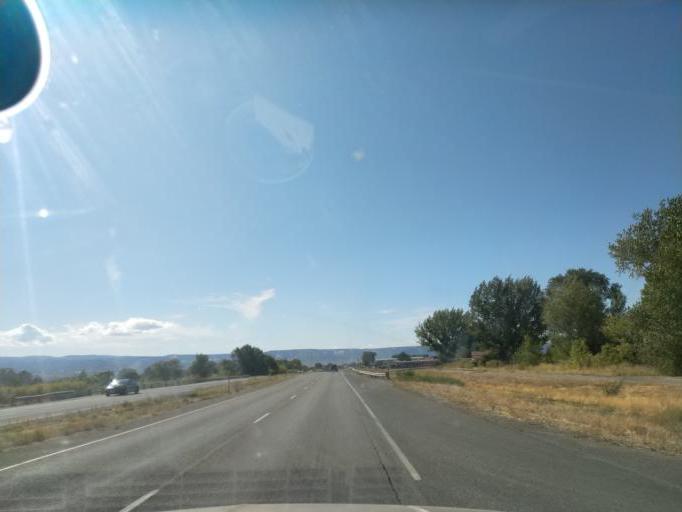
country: US
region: Colorado
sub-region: Mesa County
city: Fruitvale
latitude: 39.0803
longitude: -108.4850
